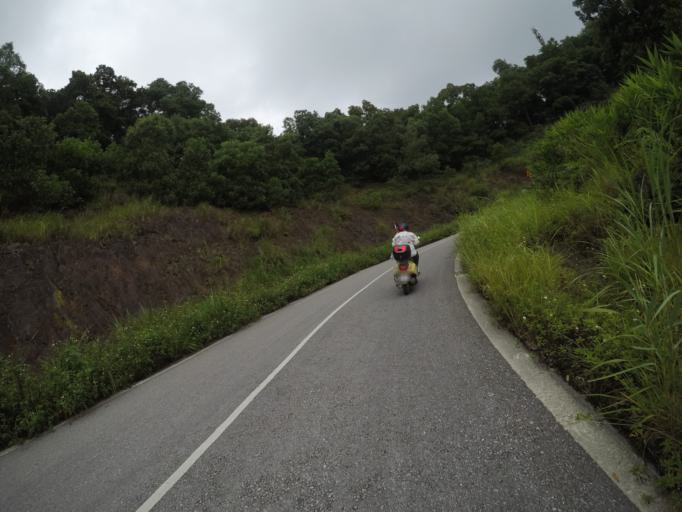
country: VN
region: Ha Noi
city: Soc Son
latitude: 21.2885
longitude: 105.8239
